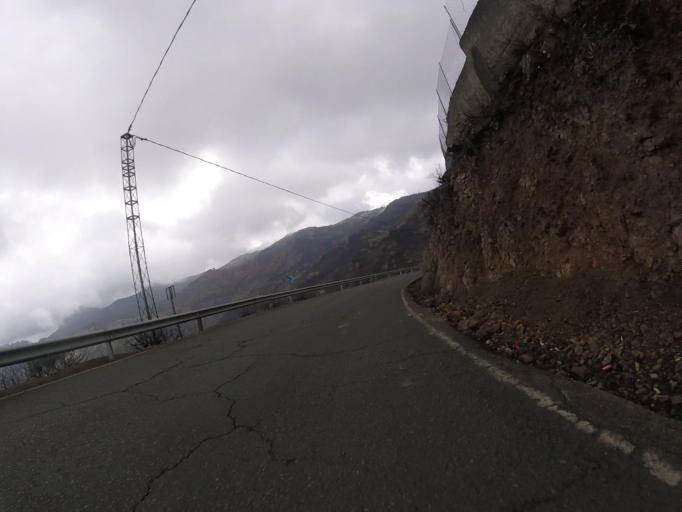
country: ES
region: Canary Islands
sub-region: Provincia de Las Palmas
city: Tejeda
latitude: 27.9892
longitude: -15.5757
